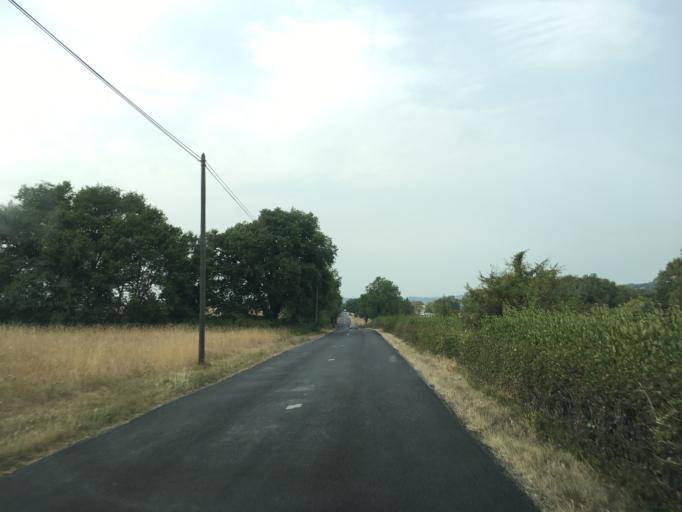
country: FR
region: Midi-Pyrenees
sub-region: Departement du Lot
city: Souillac
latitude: 44.8275
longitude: 1.5688
